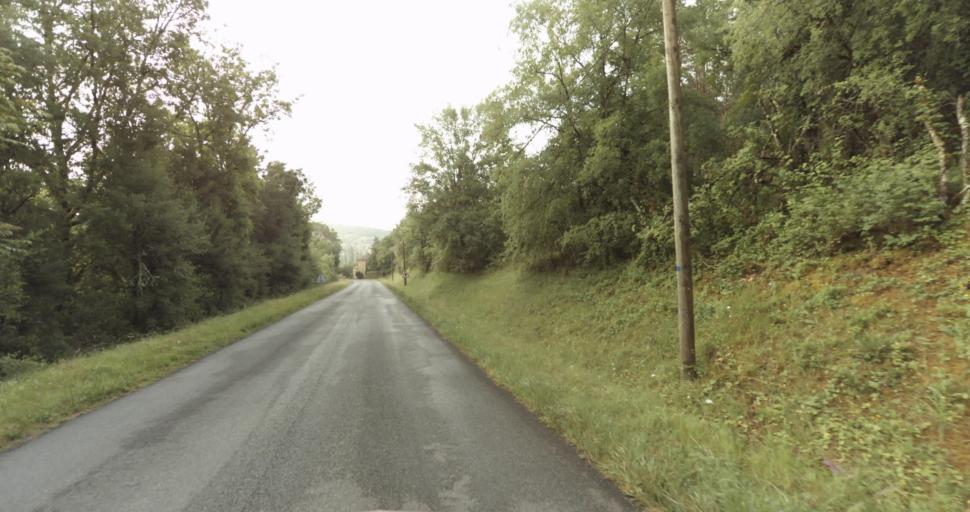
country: FR
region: Aquitaine
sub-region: Departement de la Dordogne
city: Lalinde
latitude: 44.9136
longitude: 0.8020
